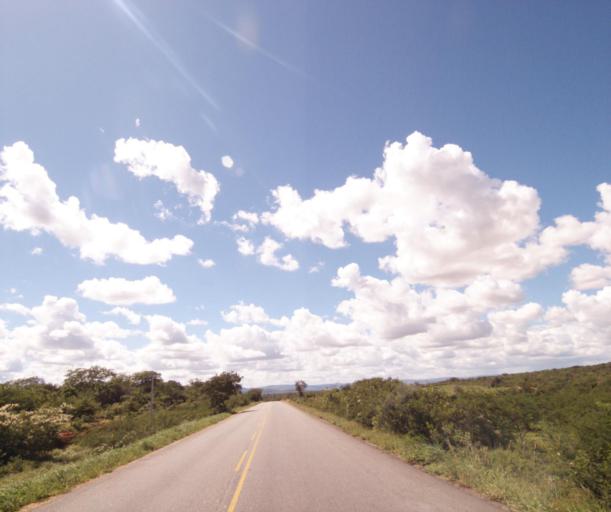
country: BR
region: Bahia
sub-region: Cacule
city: Cacule
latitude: -14.1836
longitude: -42.1641
